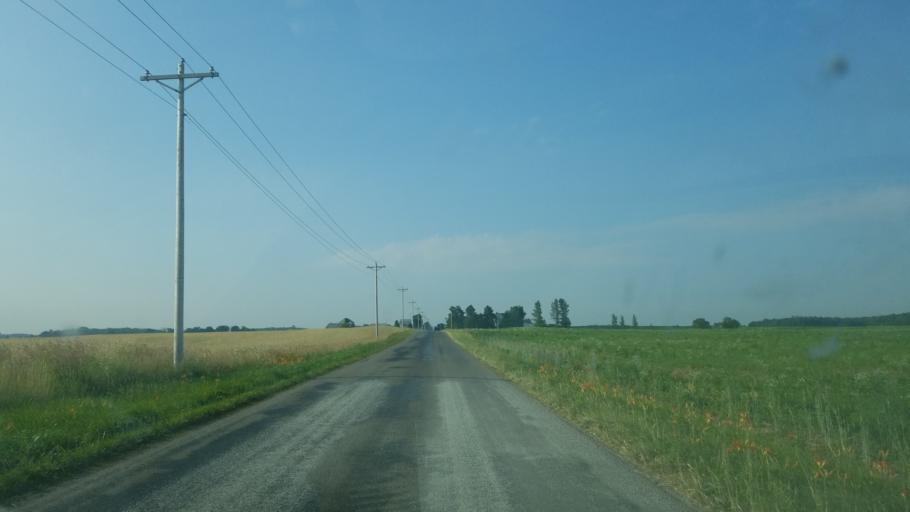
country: US
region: Ohio
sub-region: Hardin County
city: Kenton
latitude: 40.6213
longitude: -83.7202
